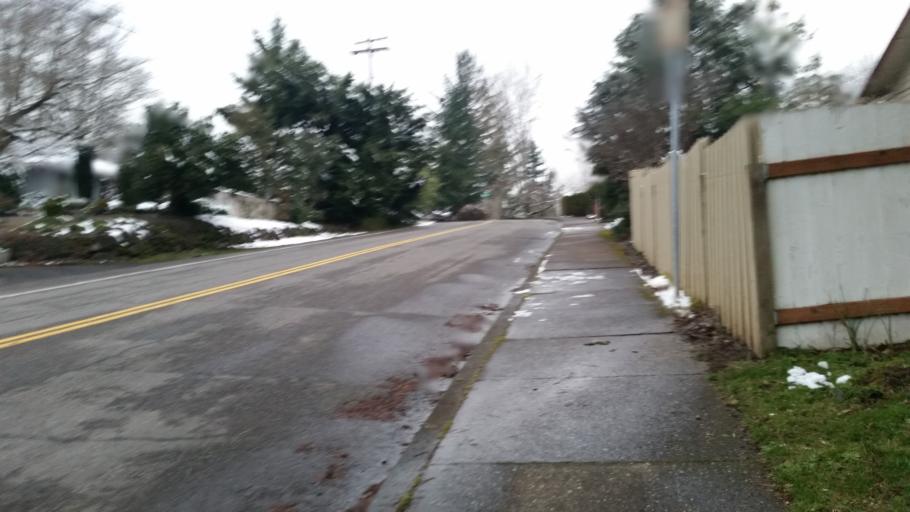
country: US
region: Oregon
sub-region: Washington County
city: Garden Home-Whitford
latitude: 45.4772
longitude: -122.7129
